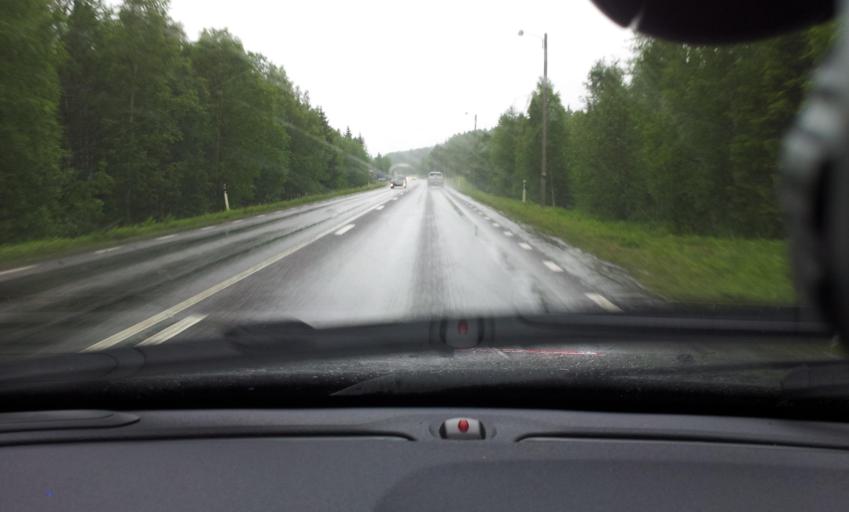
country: SE
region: Jaemtland
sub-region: Are Kommun
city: Are
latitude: 63.3351
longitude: 13.2140
